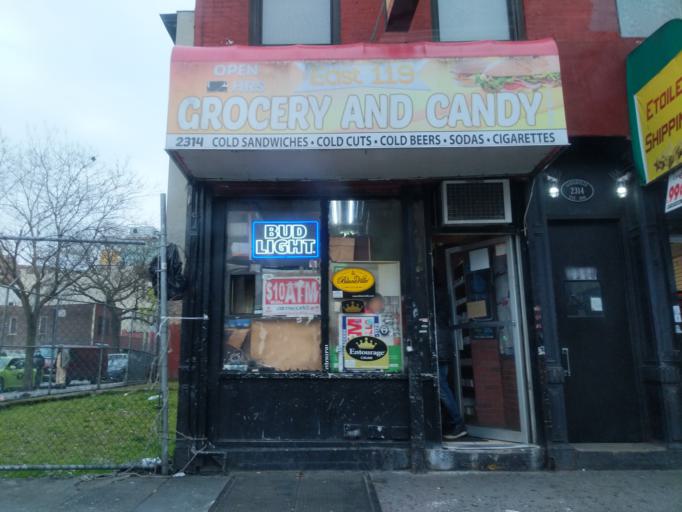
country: US
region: New York
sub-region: New York County
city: Manhattan
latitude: 40.7977
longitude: -73.9340
